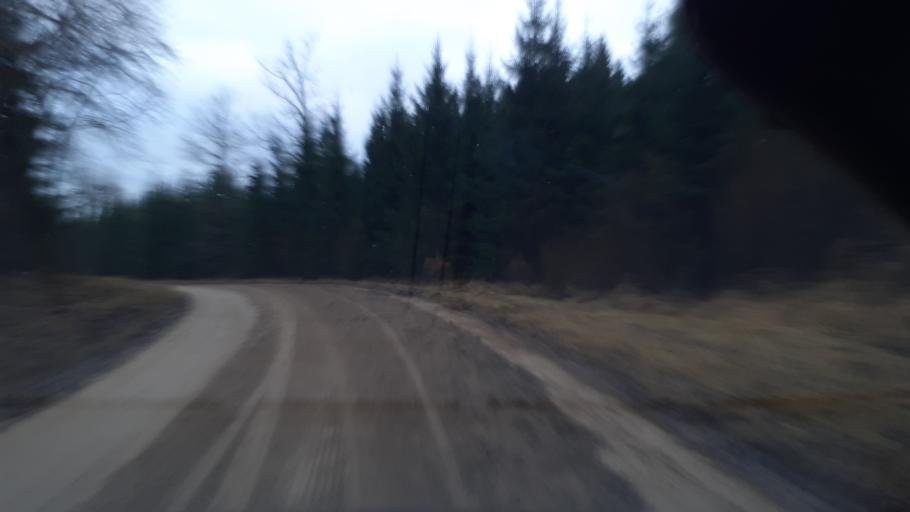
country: LV
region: Kuldigas Rajons
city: Kuldiga
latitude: 56.9148
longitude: 21.7690
